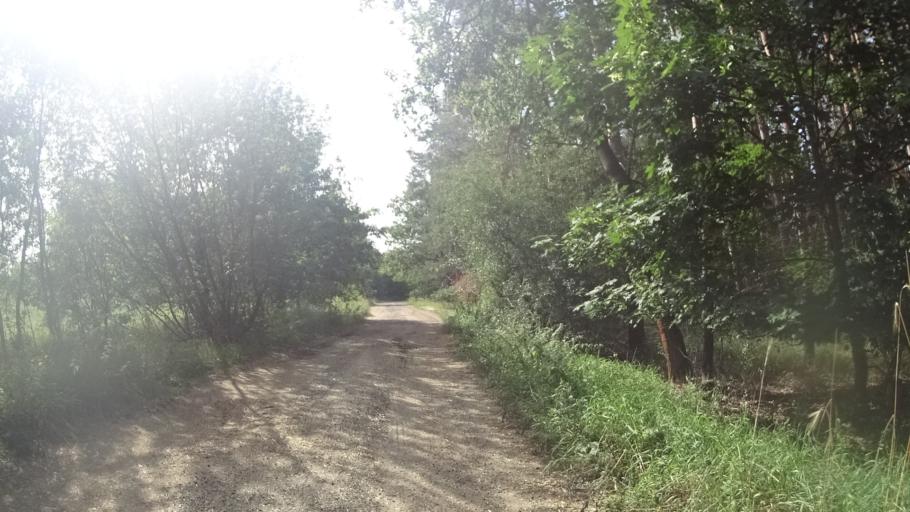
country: DE
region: Brandenburg
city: Brandenburg an der Havel
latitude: 52.3693
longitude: 12.6249
